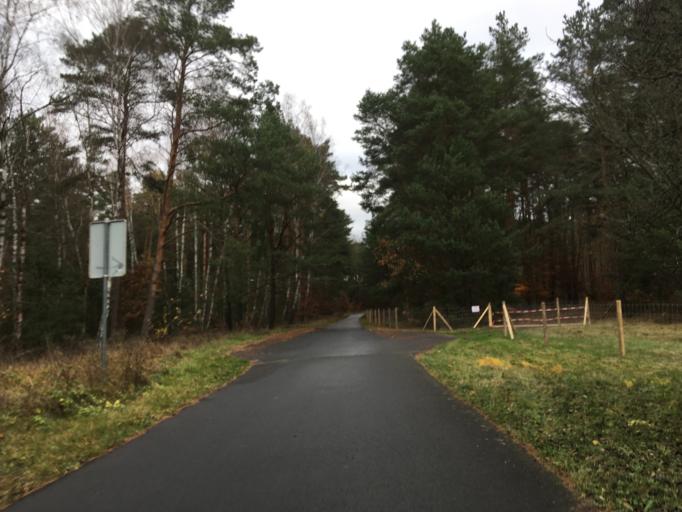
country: DE
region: Brandenburg
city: Jamlitz
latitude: 52.0320
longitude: 14.4683
